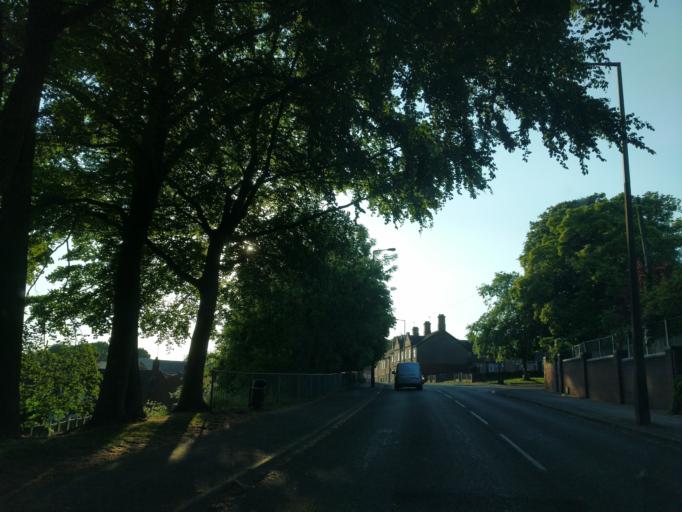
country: GB
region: England
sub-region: Staffordshire
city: Stone
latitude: 52.8999
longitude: -2.1403
